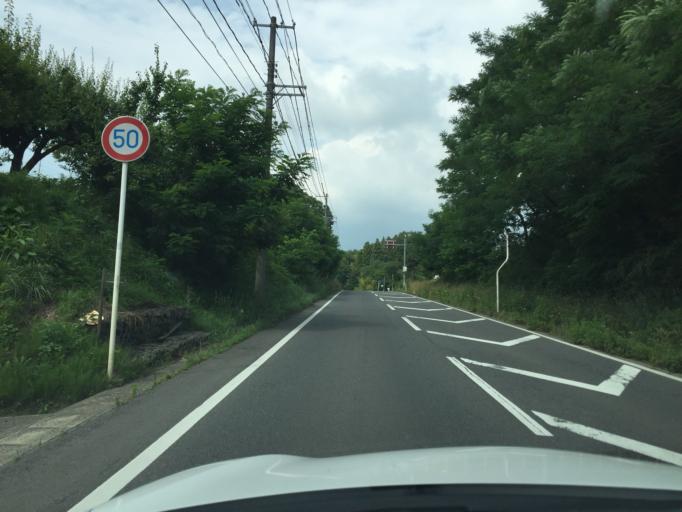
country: JP
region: Fukushima
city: Sukagawa
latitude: 37.2761
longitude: 140.4210
